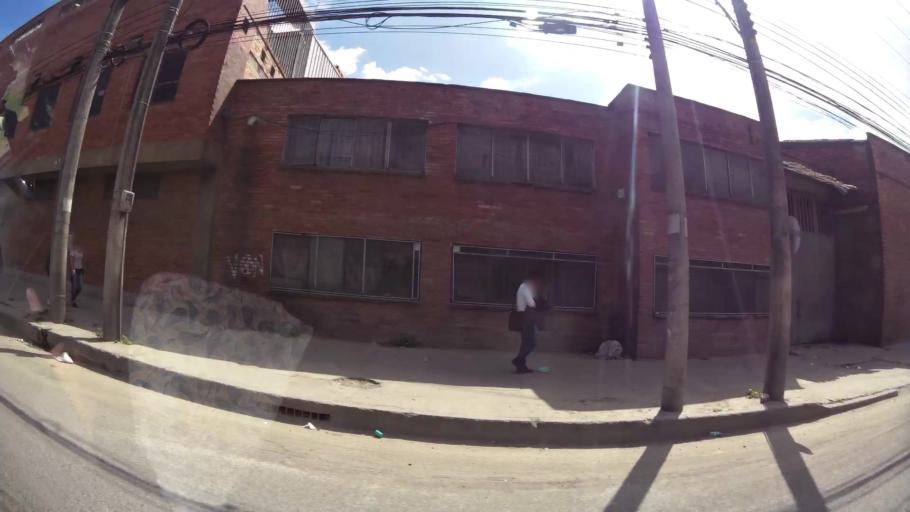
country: CO
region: Bogota D.C.
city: Bogota
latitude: 4.6376
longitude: -74.1136
